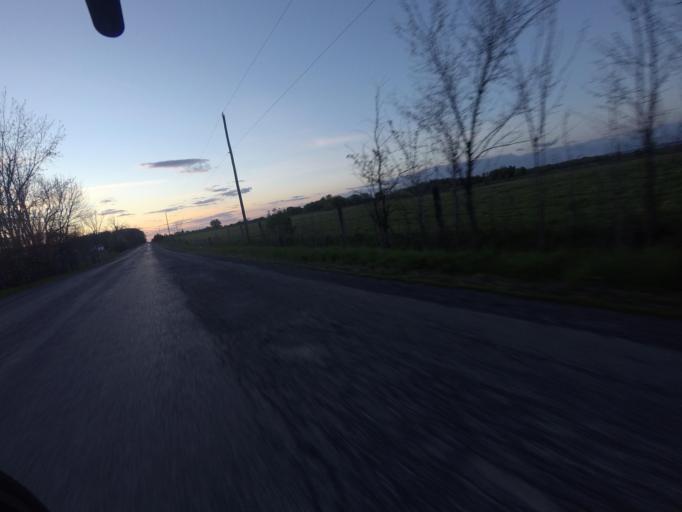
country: CA
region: Ontario
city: Arnprior
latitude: 45.4163
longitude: -76.2204
